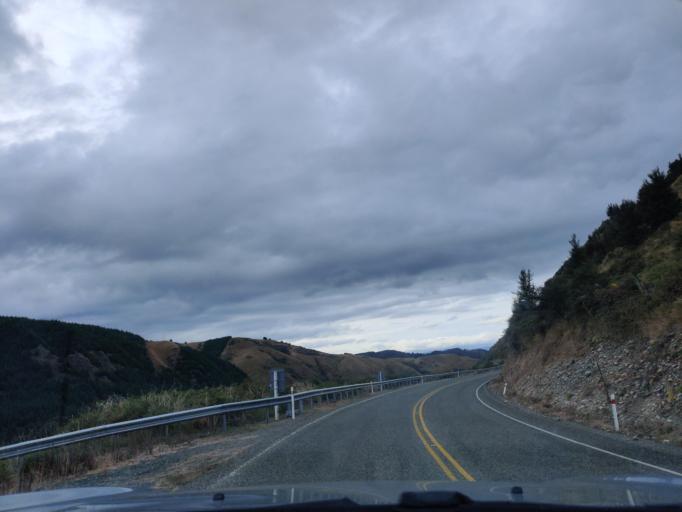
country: NZ
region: Tasman
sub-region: Tasman District
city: Wakefield
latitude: -41.7034
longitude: 172.6675
